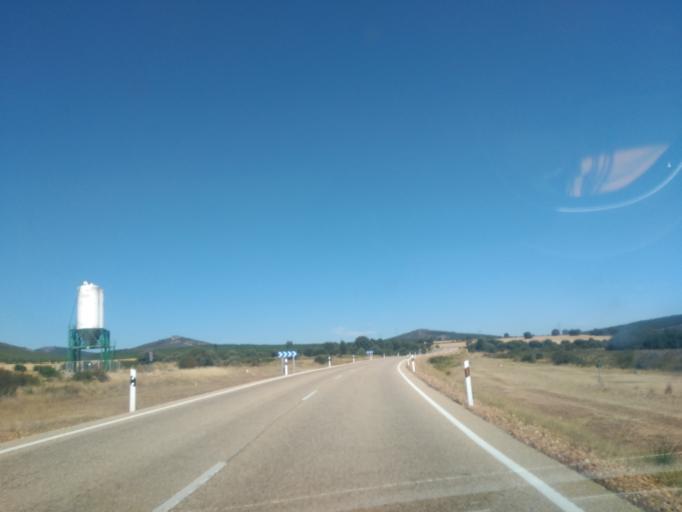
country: ES
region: Castille and Leon
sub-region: Provincia de Zamora
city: Tabara
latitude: 41.8547
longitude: -5.9921
